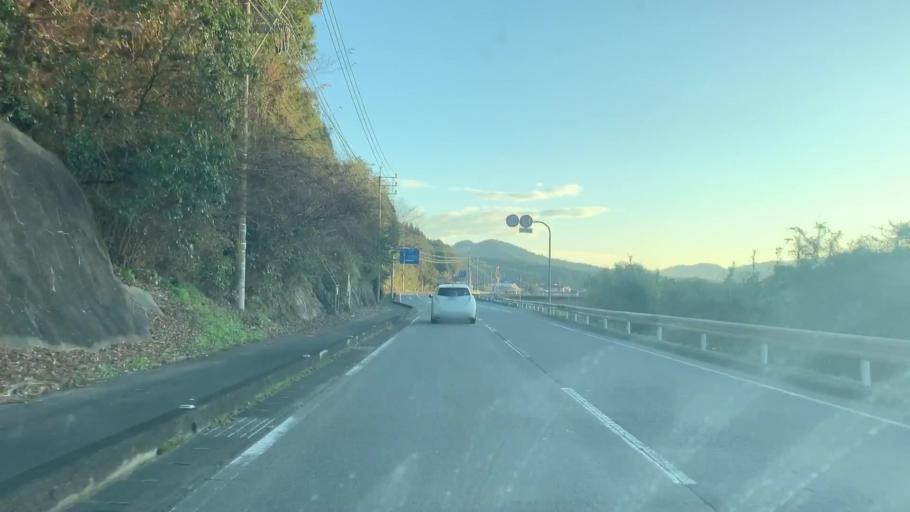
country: JP
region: Saga Prefecture
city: Imaricho-ko
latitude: 33.2726
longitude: 129.9647
